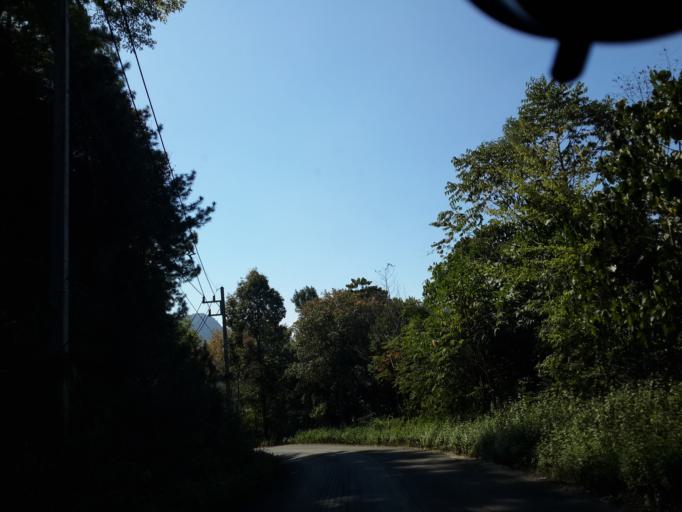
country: TH
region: Chiang Mai
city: Fang
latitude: 19.9008
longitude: 99.0471
